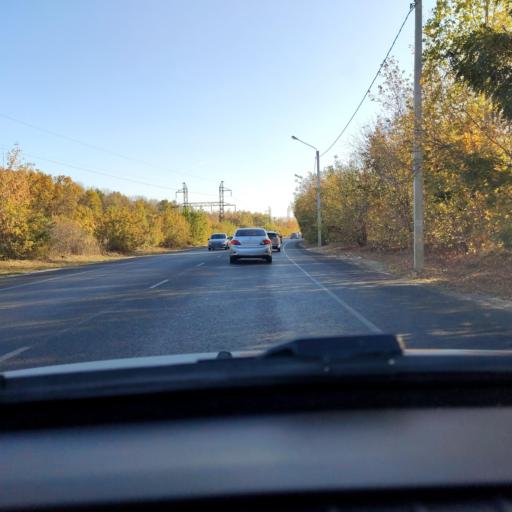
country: RU
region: Voronezj
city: Voronezh
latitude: 51.6096
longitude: 39.1795
